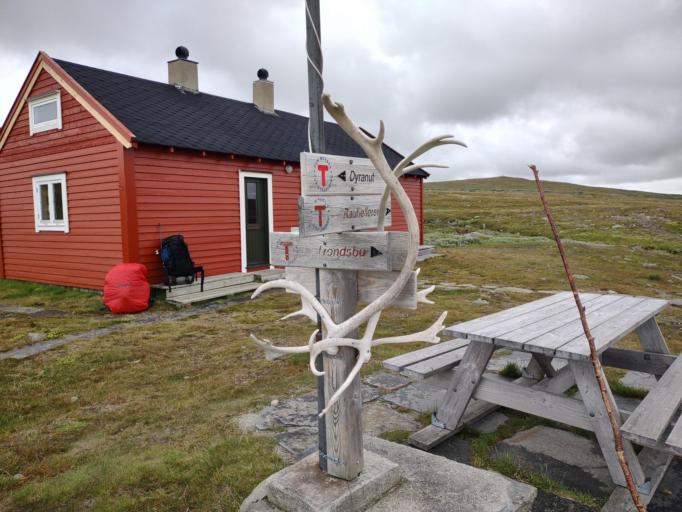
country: NO
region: Buskerud
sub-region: Hol
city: Geilo
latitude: 60.2976
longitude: 7.6554
